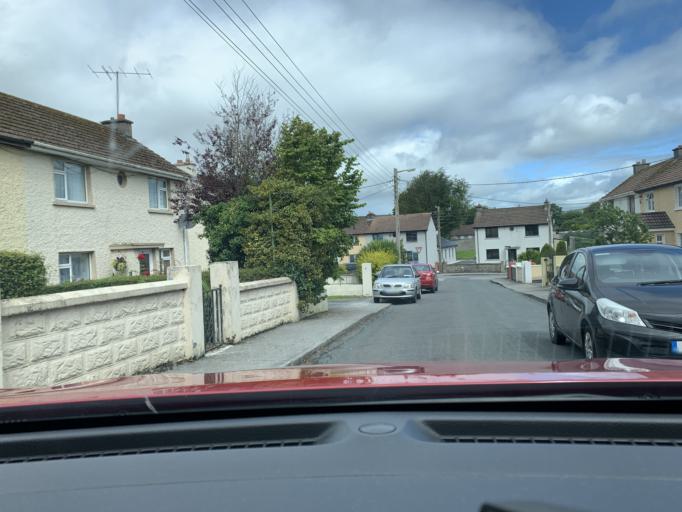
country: IE
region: Connaught
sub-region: Roscommon
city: Boyle
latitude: 53.9699
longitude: -8.2972
